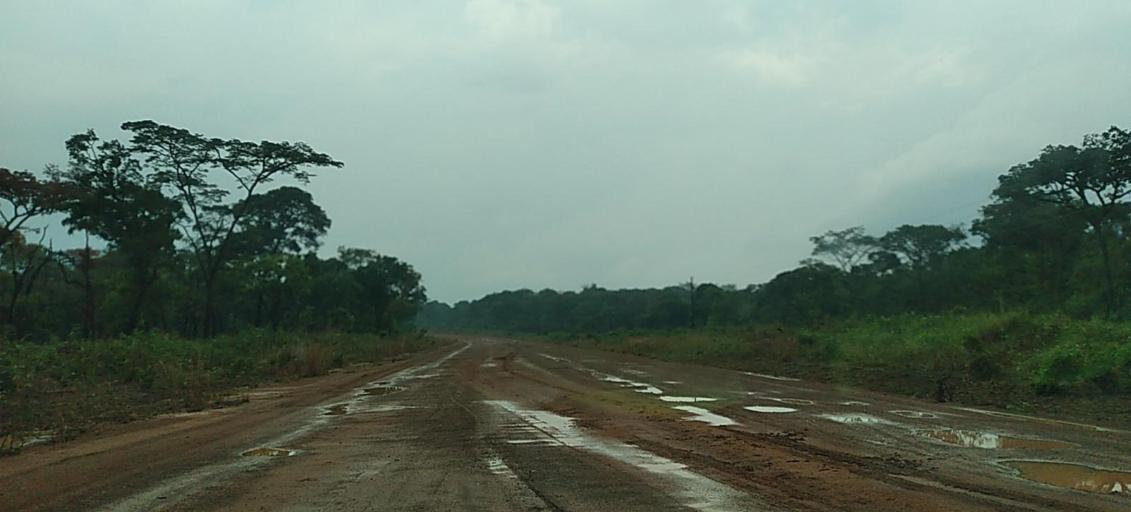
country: ZM
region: North-Western
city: Mwinilunga
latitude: -11.5857
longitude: 24.3880
